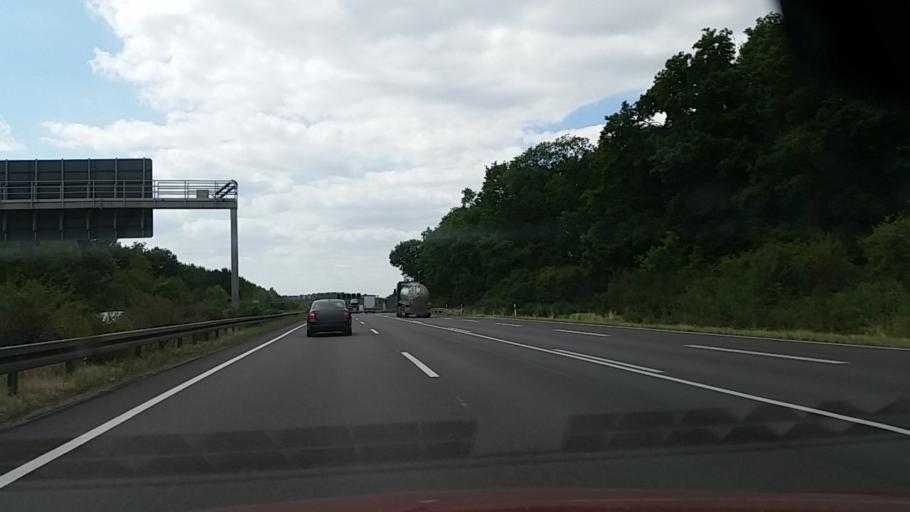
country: DE
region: Lower Saxony
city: Lehre
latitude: 52.3078
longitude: 10.7178
